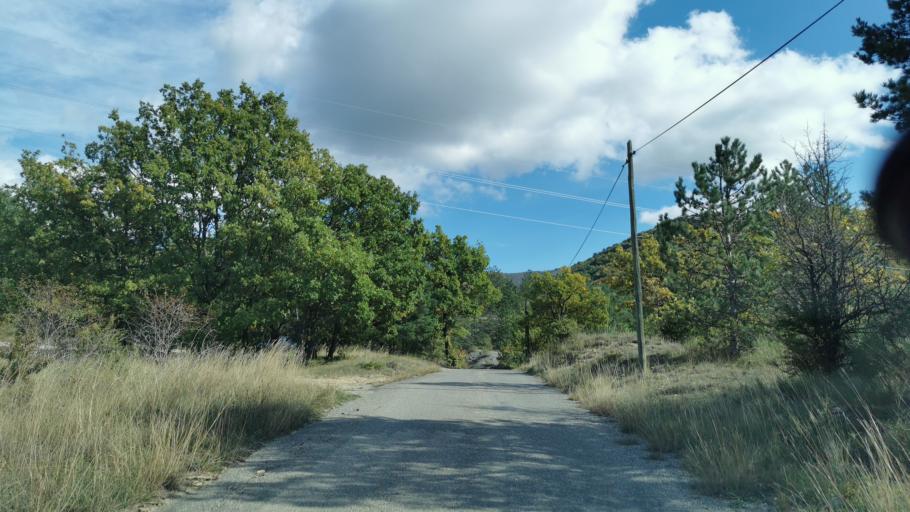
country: FR
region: Provence-Alpes-Cote d'Azur
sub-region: Departement des Alpes-de-Haute-Provence
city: Volonne
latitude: 44.1837
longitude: 6.0249
